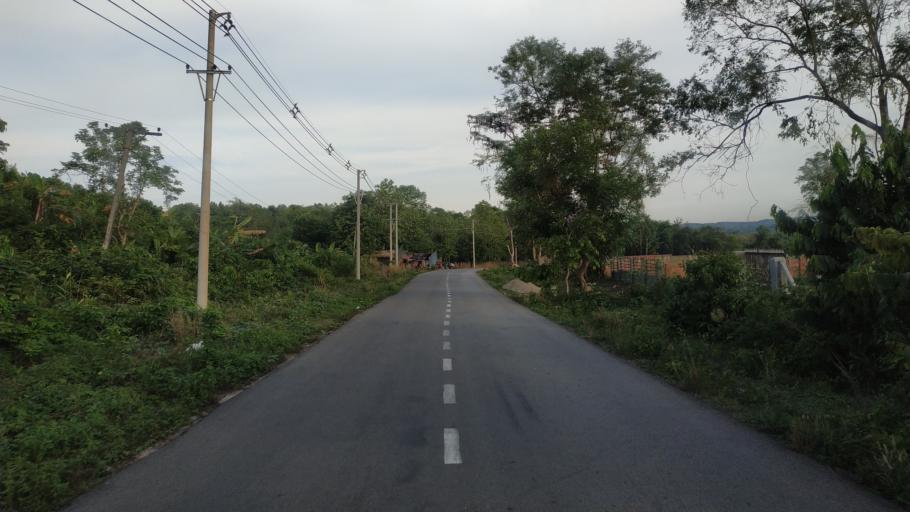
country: MM
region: Mon
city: Kyaikto
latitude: 17.4140
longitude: 97.0721
